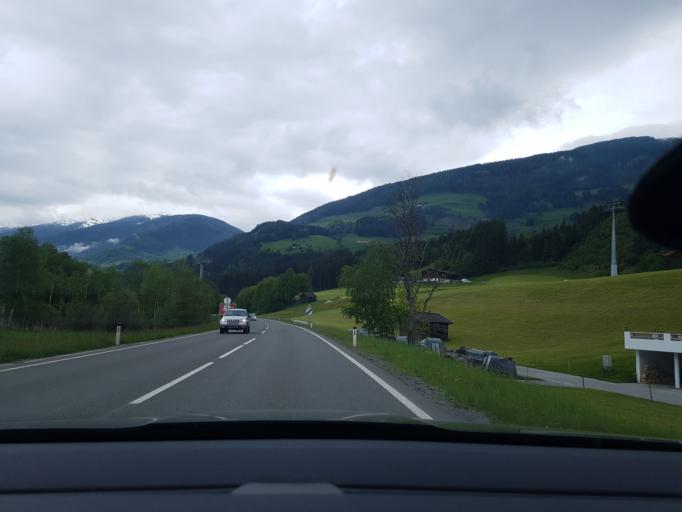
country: AT
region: Salzburg
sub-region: Politischer Bezirk Zell am See
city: Hollersbach im Pinzgau
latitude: 47.2813
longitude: 12.4073
